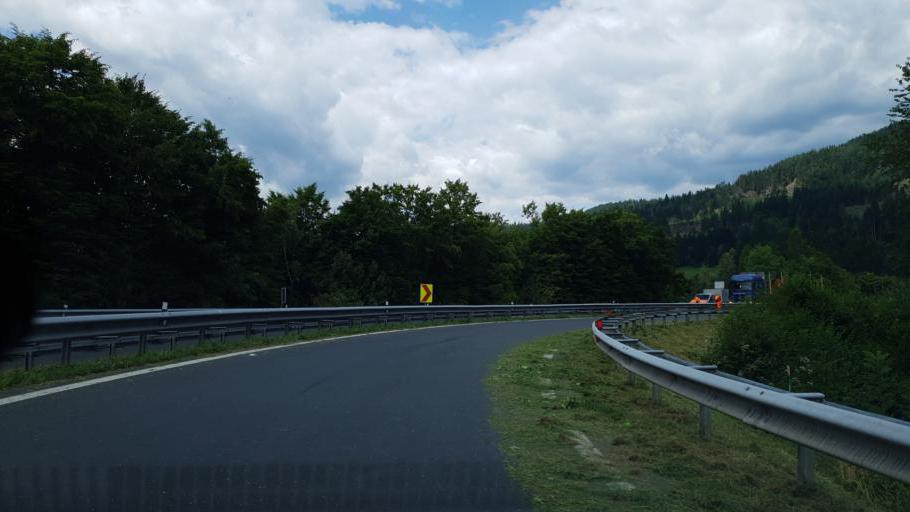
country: AT
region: Carinthia
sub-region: Politischer Bezirk Spittal an der Drau
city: Spittal an der Drau
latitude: 46.7784
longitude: 13.5381
